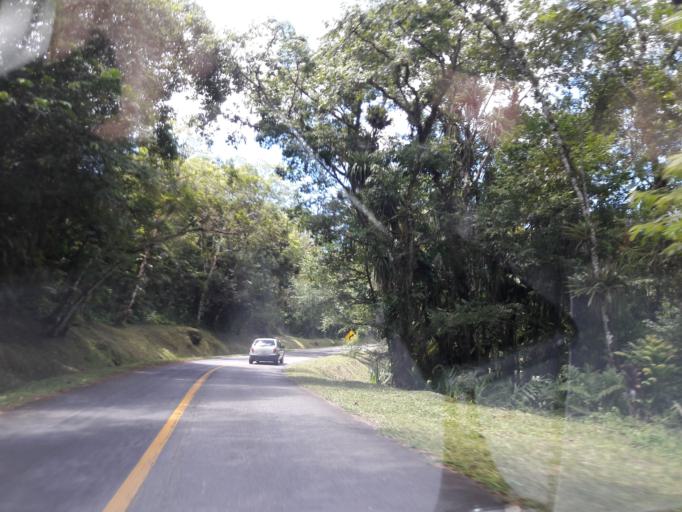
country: BR
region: Parana
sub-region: Antonina
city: Antonina
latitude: -25.4266
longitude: -48.8131
